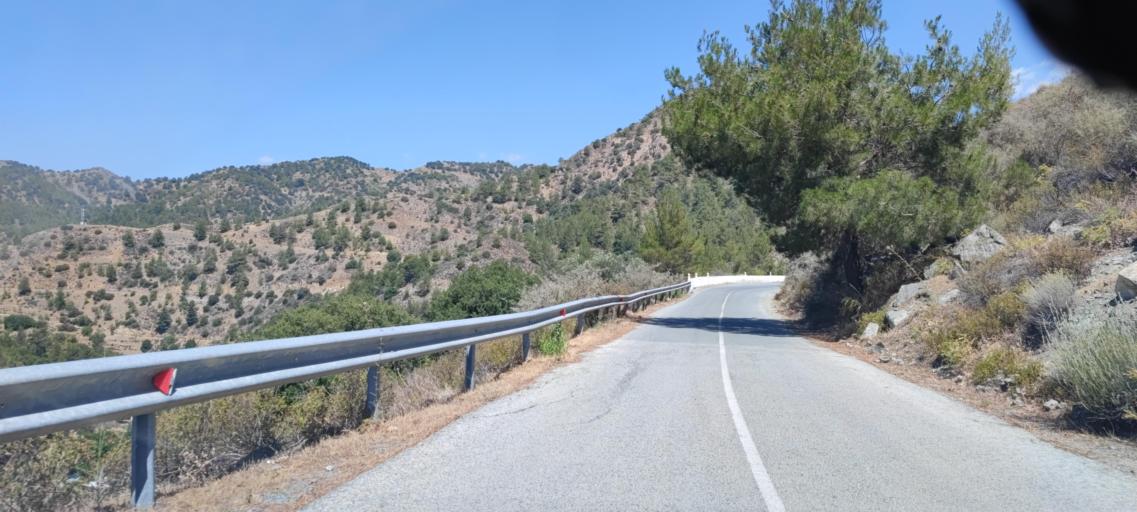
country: CY
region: Lefkosia
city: Kakopetria
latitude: 34.9237
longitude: 32.7944
